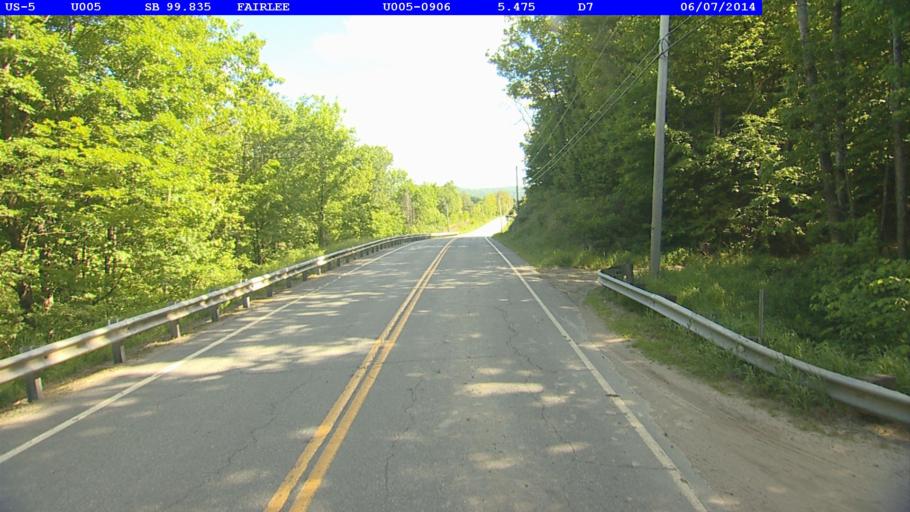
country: US
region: New Hampshire
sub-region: Grafton County
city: Orford
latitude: 43.9358
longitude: -72.1200
